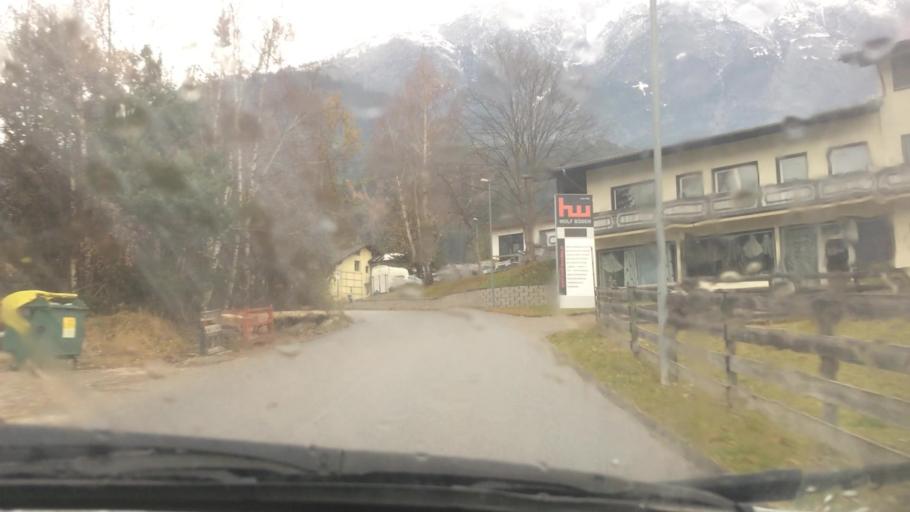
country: AT
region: Tyrol
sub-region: Politischer Bezirk Innsbruck Land
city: Pfaffenhofen
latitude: 47.3168
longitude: 11.0969
